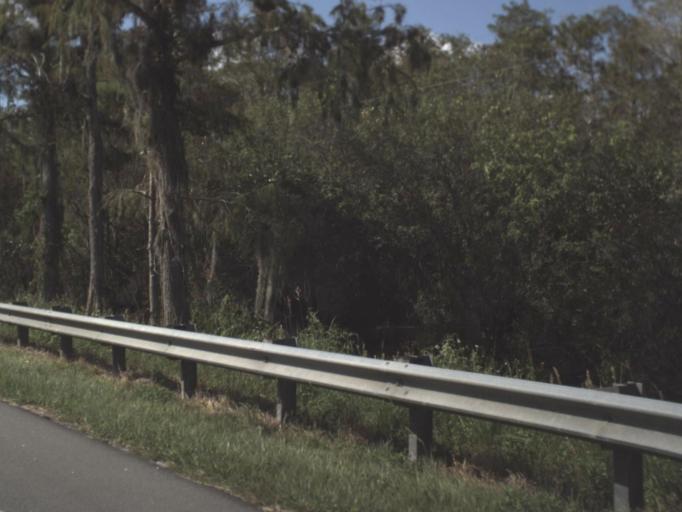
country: US
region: Florida
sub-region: Miami-Dade County
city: Kendall West
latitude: 25.8489
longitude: -80.9538
